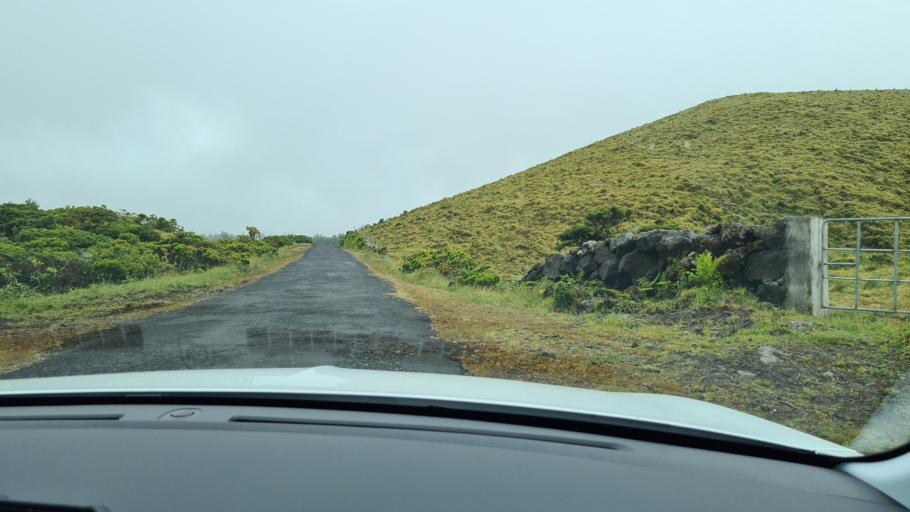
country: PT
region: Azores
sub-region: Sao Roque do Pico
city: Sao Roque do Pico
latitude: 38.4548
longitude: -28.2532
